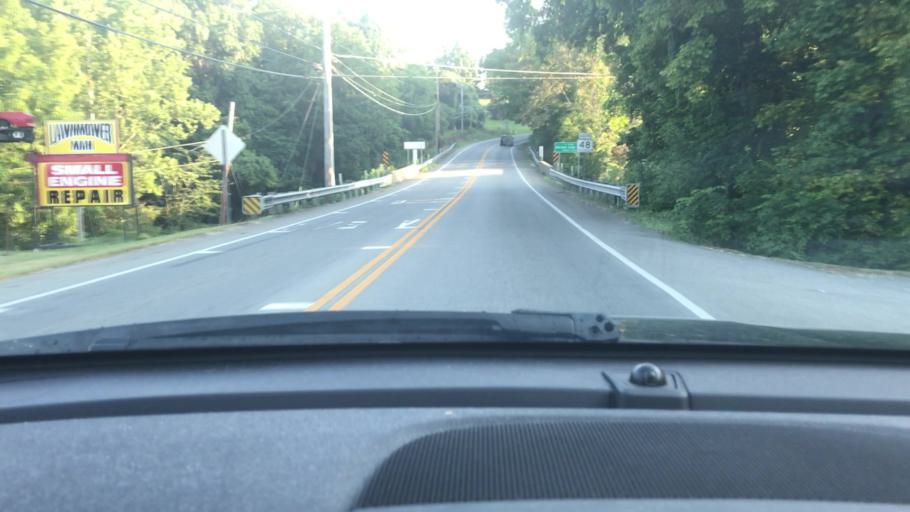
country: US
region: Tennessee
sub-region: Dickson County
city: Charlotte
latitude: 36.1759
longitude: -87.3423
